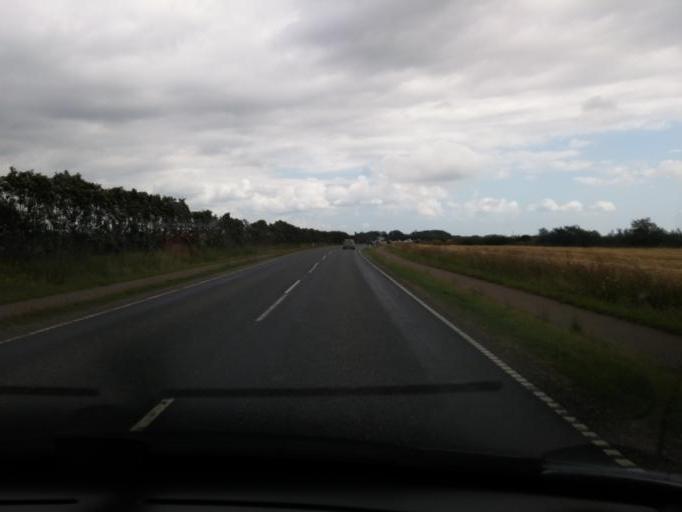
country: DK
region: South Denmark
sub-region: Langeland Kommune
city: Rudkobing
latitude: 54.9586
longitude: 10.6748
